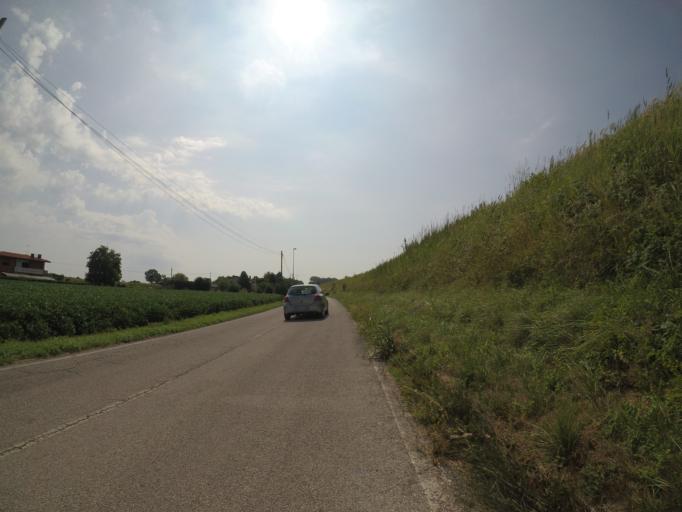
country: IT
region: Friuli Venezia Giulia
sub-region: Provincia di Udine
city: Pertegada
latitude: 45.7069
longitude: 13.0430
